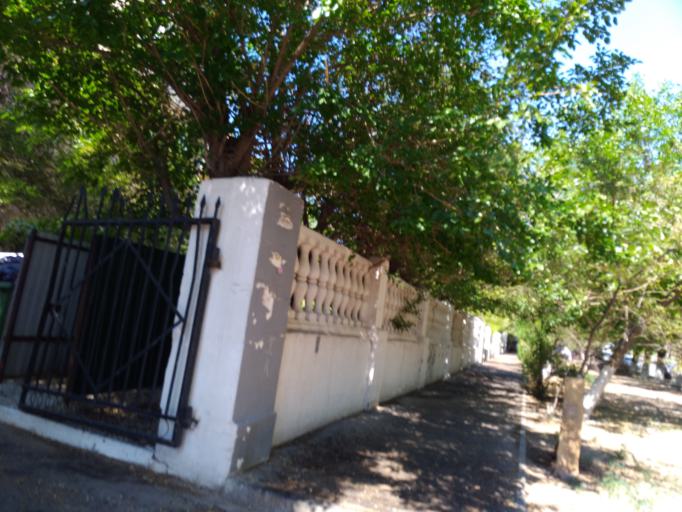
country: RU
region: Volgograd
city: Volgograd
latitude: 48.7138
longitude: 44.5096
